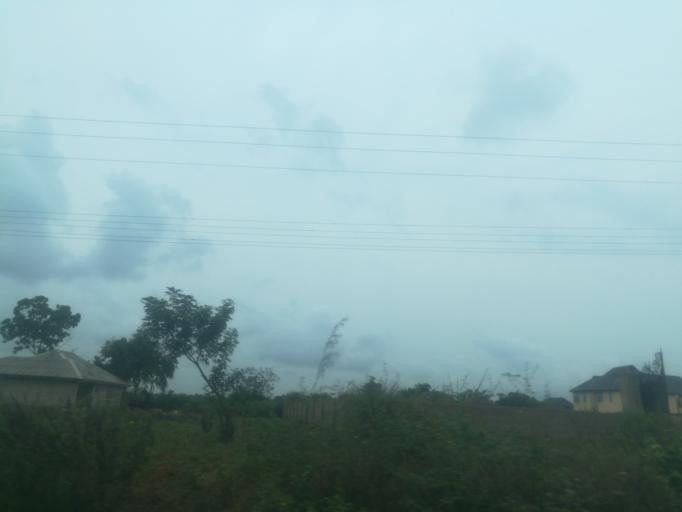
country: NG
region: Ogun
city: Ayetoro
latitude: 7.1095
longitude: 3.1336
